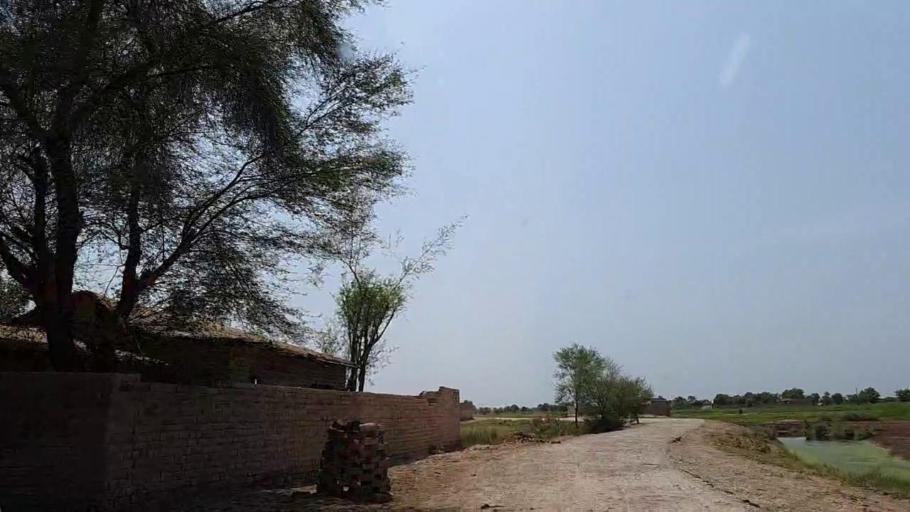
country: PK
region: Sindh
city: Adilpur
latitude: 27.9702
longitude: 69.3948
